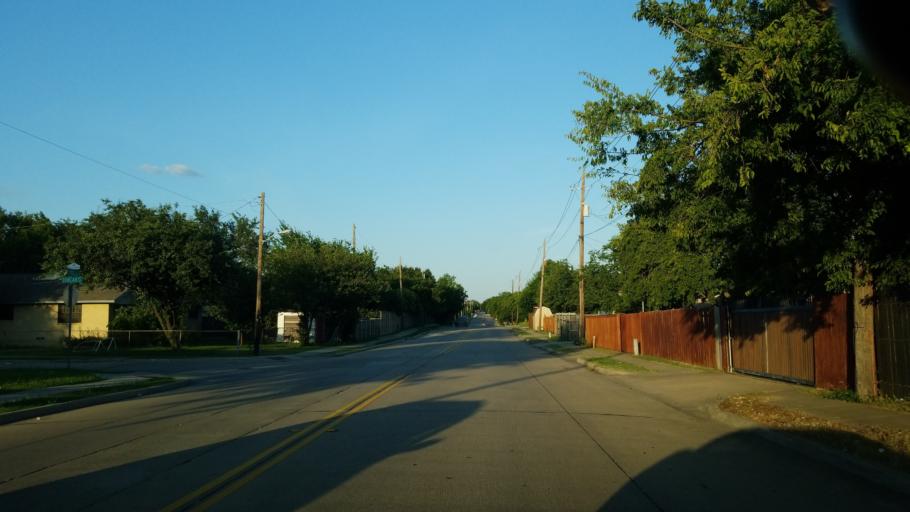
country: US
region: Texas
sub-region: Dallas County
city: Carrollton
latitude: 32.9463
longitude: -96.8863
